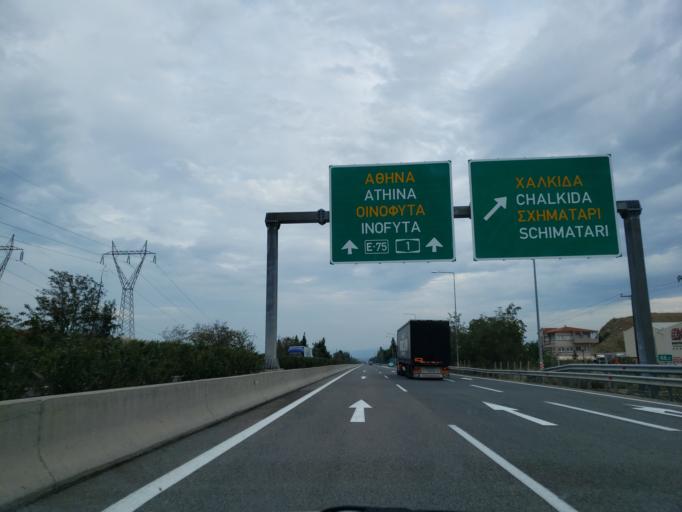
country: GR
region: Central Greece
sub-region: Nomos Voiotias
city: Schimatari
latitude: 38.3571
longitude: 23.5650
